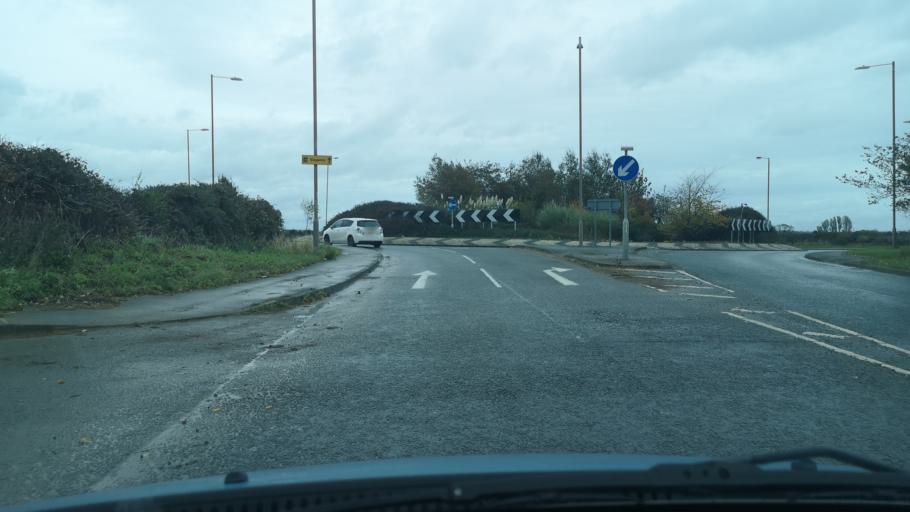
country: GB
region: England
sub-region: City and Borough of Wakefield
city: Hemsworth
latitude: 53.6270
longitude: -1.3391
